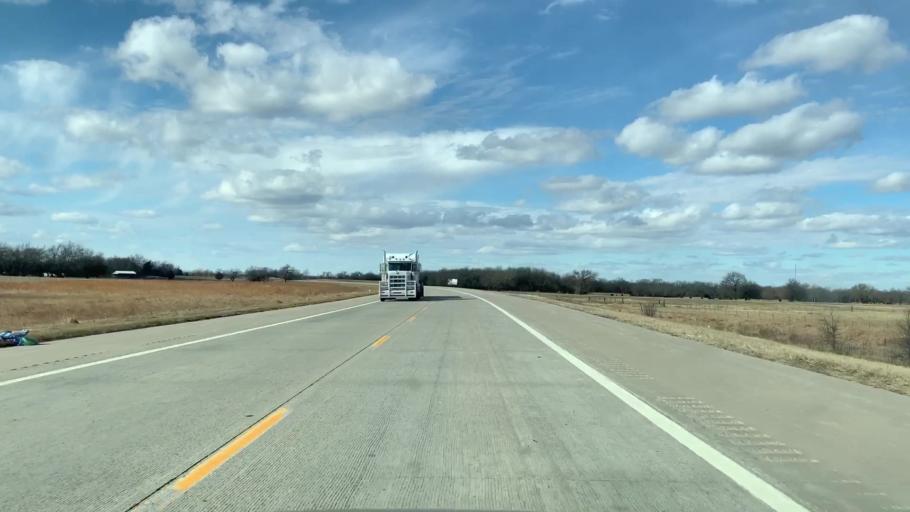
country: US
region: Kansas
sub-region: Labette County
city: Parsons
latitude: 37.3570
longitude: -95.2165
